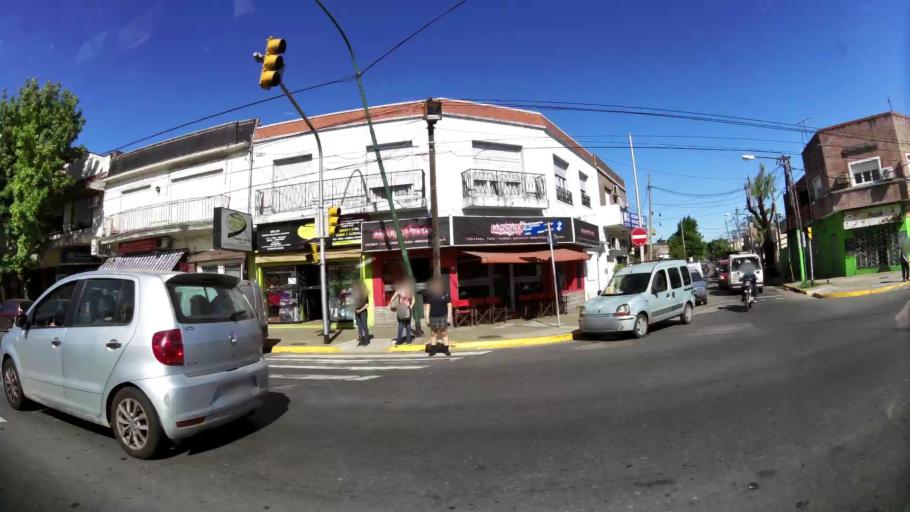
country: AR
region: Buenos Aires
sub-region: Partido de San Isidro
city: San Isidro
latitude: -34.5119
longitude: -58.5672
